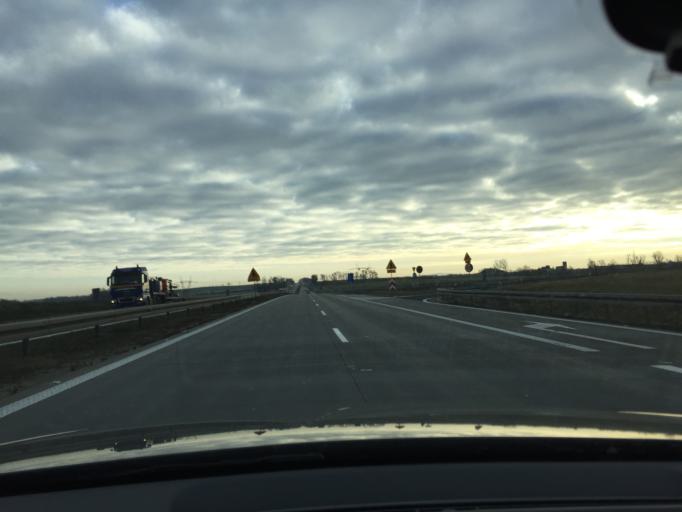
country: PL
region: Lower Silesian Voivodeship
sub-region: Powiat legnicki
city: Legnickie Pole
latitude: 51.1418
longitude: 16.2781
